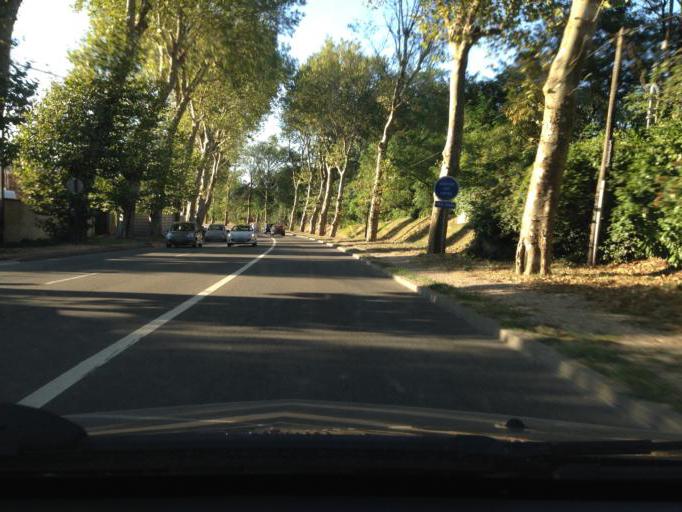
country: FR
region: Ile-de-France
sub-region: Departement des Yvelines
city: Louveciennes
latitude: 48.8683
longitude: 2.1129
